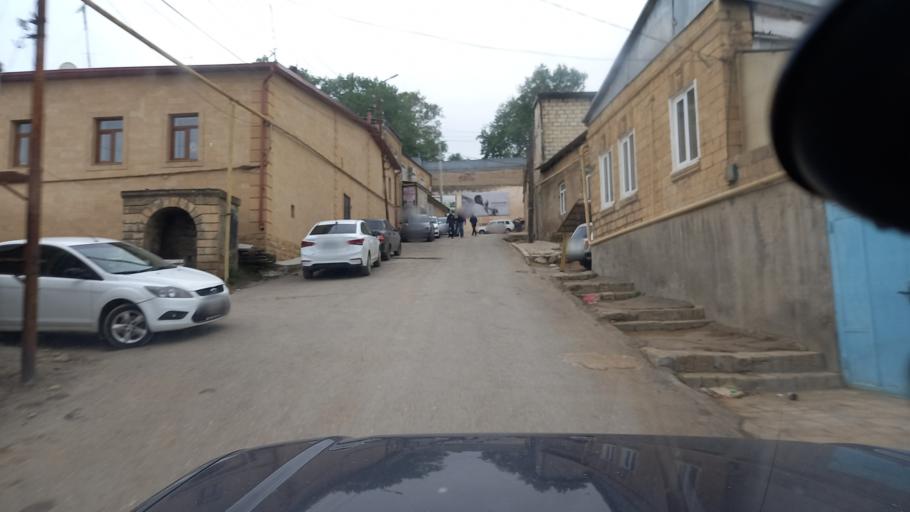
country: RU
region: Dagestan
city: Derbent
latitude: 42.0559
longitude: 48.2810
